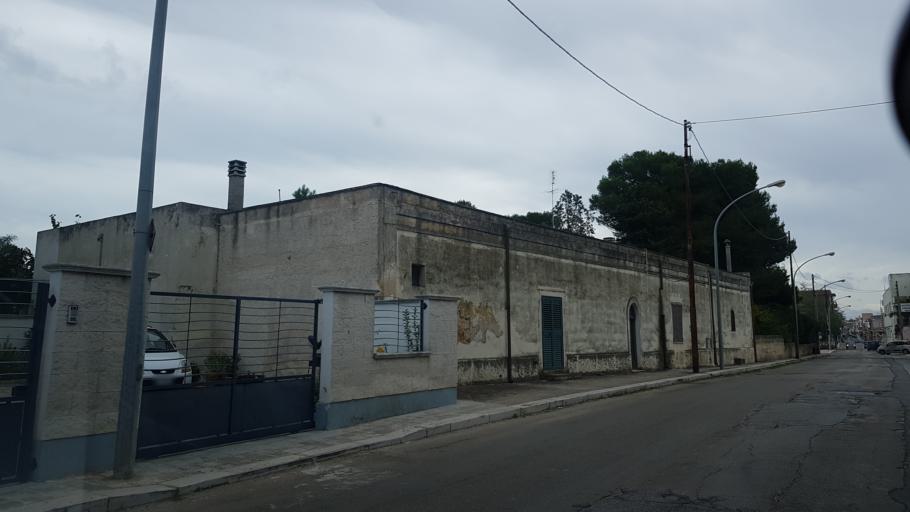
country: IT
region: Apulia
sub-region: Provincia di Brindisi
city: Mesagne
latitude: 40.5656
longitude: 17.8025
